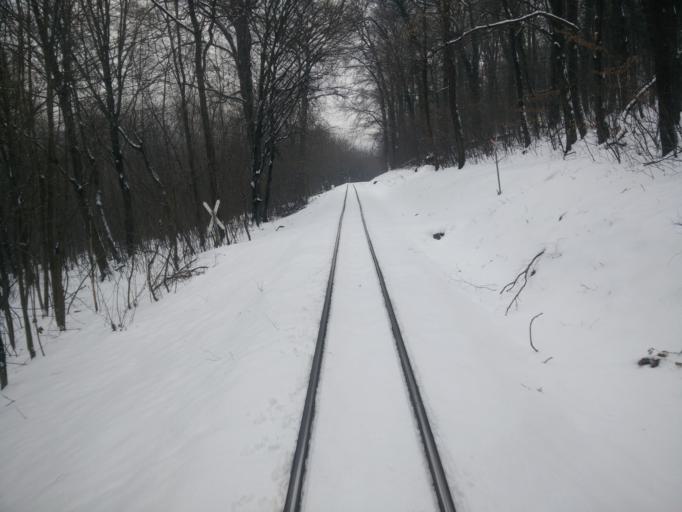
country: HU
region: Pest
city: Budakeszi
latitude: 47.5389
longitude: 18.9548
